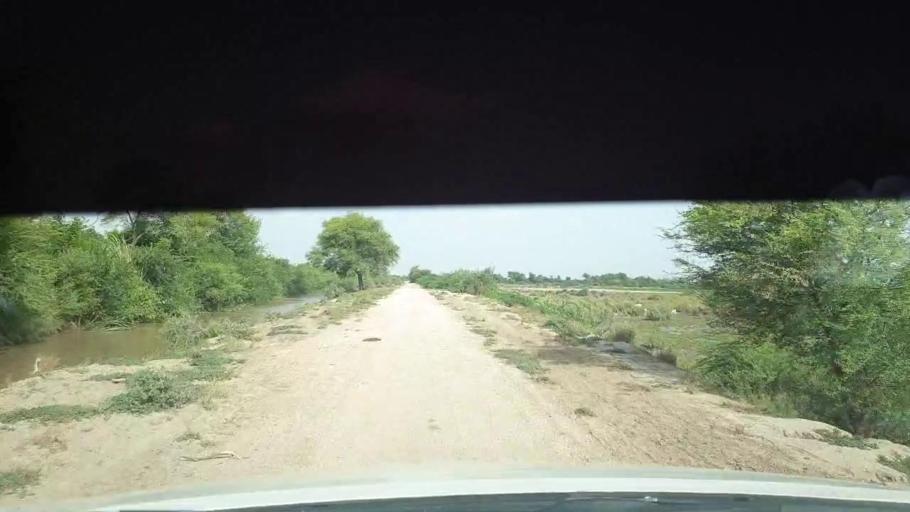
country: PK
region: Sindh
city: Kadhan
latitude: 24.5178
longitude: 69.0067
